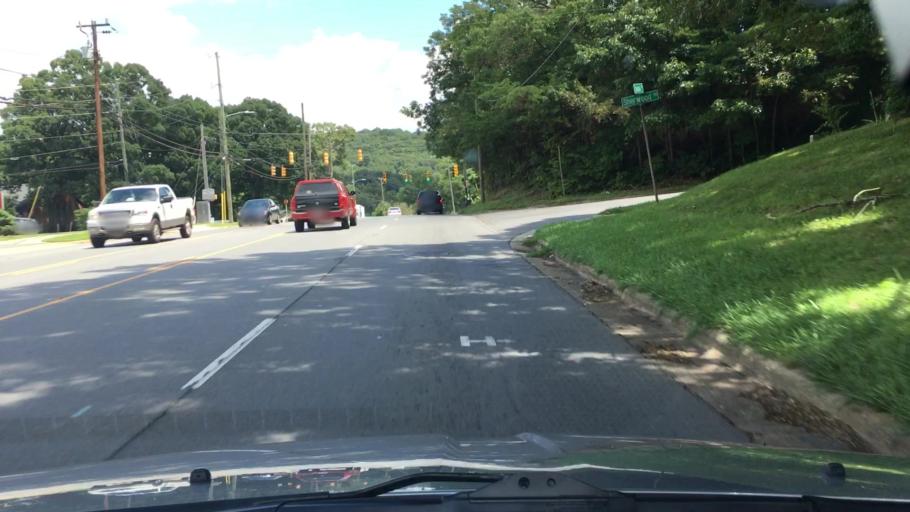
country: US
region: North Carolina
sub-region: Buncombe County
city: Asheville
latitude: 35.5885
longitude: -82.5008
